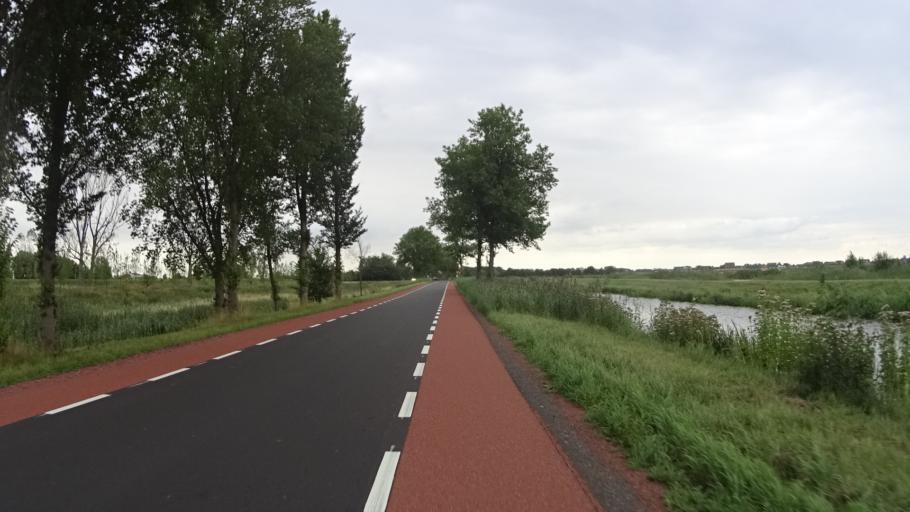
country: NL
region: Groningen
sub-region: Gemeente Groningen
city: Oosterpark
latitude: 53.2329
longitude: 6.6411
